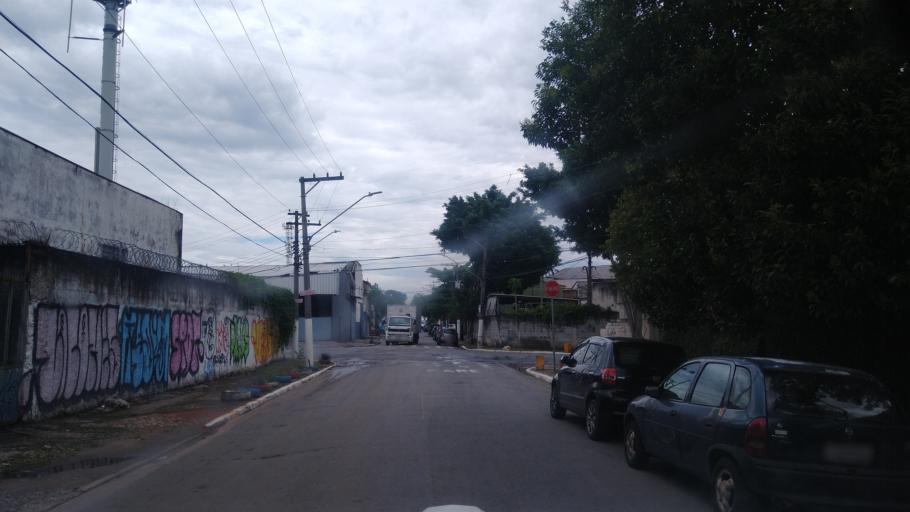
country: BR
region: Sao Paulo
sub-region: Guarulhos
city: Guarulhos
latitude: -23.5215
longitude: -46.5649
